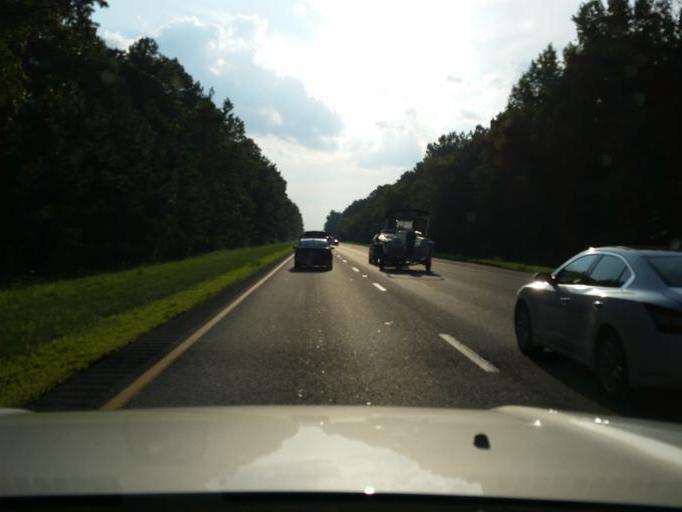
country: US
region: Virginia
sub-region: New Kent County
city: New Kent
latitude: 37.4992
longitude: -77.0493
